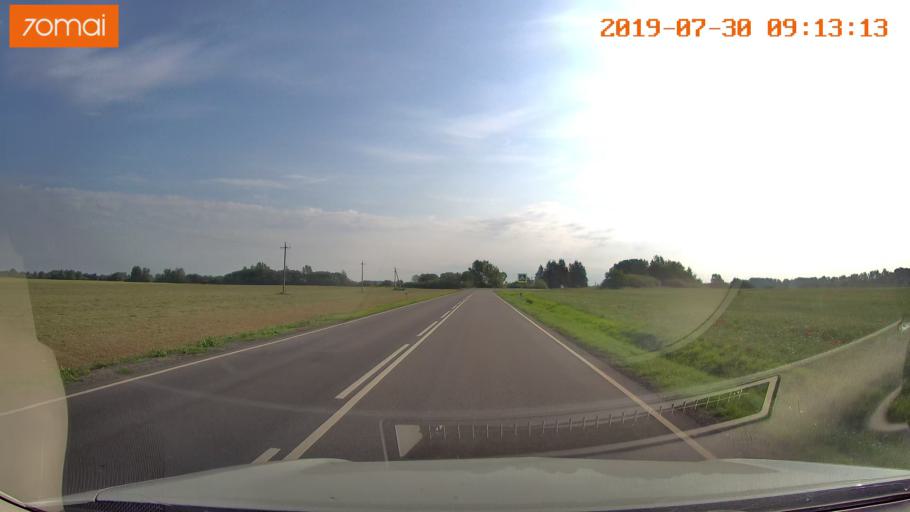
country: RU
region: Kaliningrad
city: Nesterov
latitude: 54.6236
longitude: 22.4925
